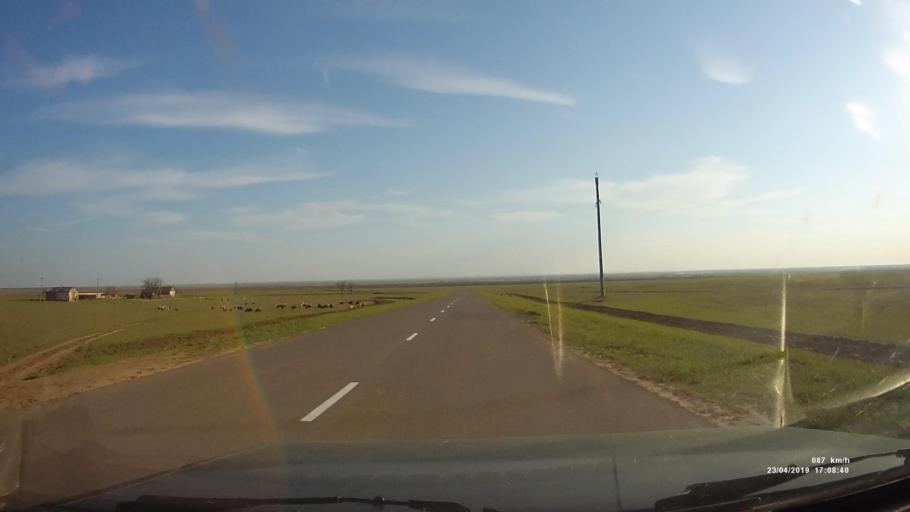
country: RU
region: Kalmykiya
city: Priyutnoye
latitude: 46.2684
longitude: 43.4858
